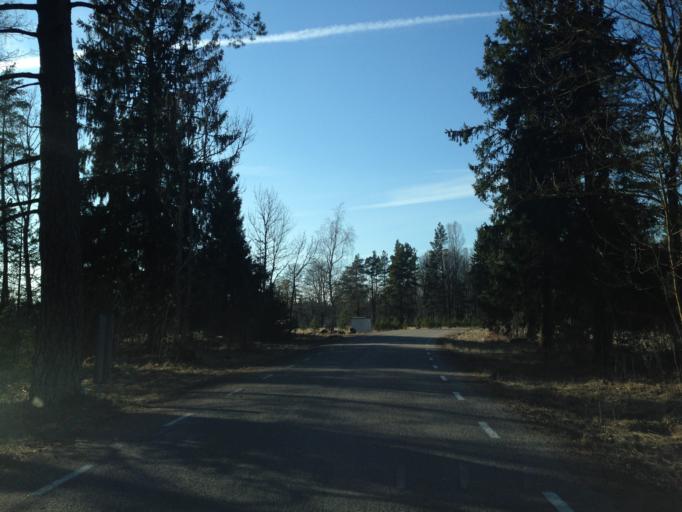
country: EE
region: Harju
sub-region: Nissi vald
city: Turba
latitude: 59.1429
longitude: 24.1595
